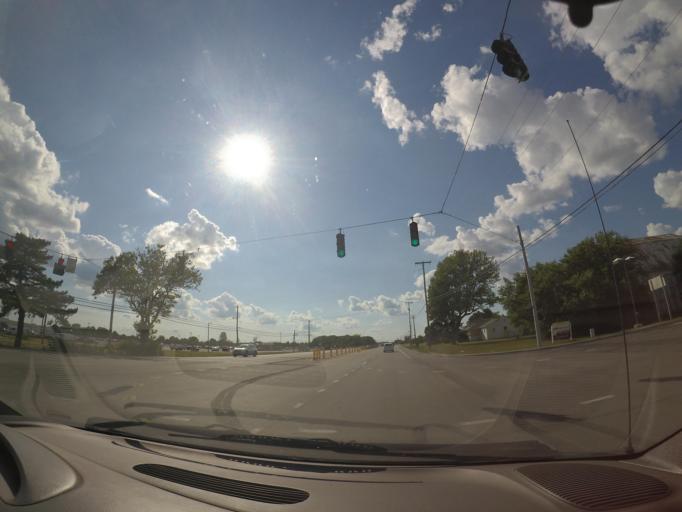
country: US
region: Ohio
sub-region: Wood County
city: Perrysburg
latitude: 41.5410
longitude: -83.5807
